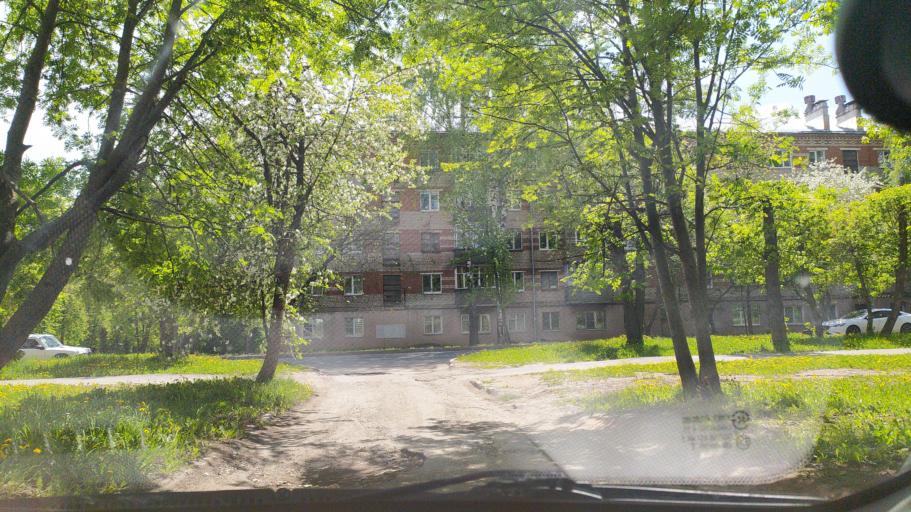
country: RU
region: Chuvashia
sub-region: Cheboksarskiy Rayon
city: Cheboksary
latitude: 56.1429
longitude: 47.2169
